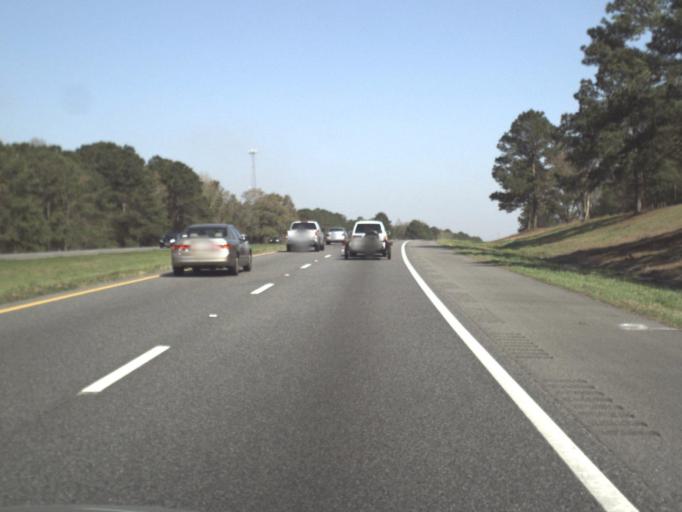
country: US
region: Florida
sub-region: Gadsden County
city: Quincy
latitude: 30.5306
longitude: -84.5381
